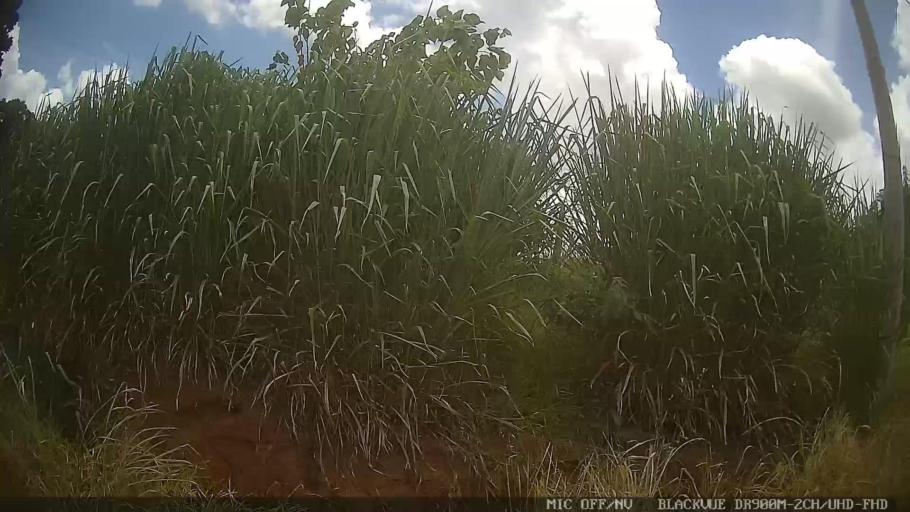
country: BR
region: Sao Paulo
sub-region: Braganca Paulista
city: Braganca Paulista
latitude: -23.0255
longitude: -46.5300
